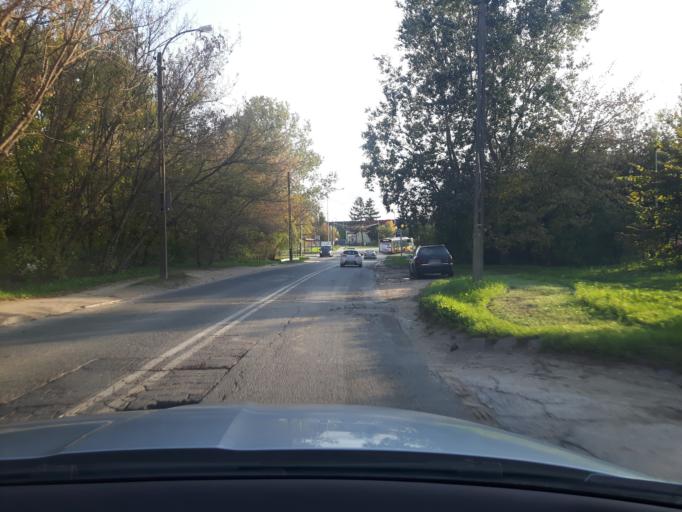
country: PL
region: Masovian Voivodeship
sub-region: Warszawa
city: Wlochy
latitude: 52.1589
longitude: 20.9923
